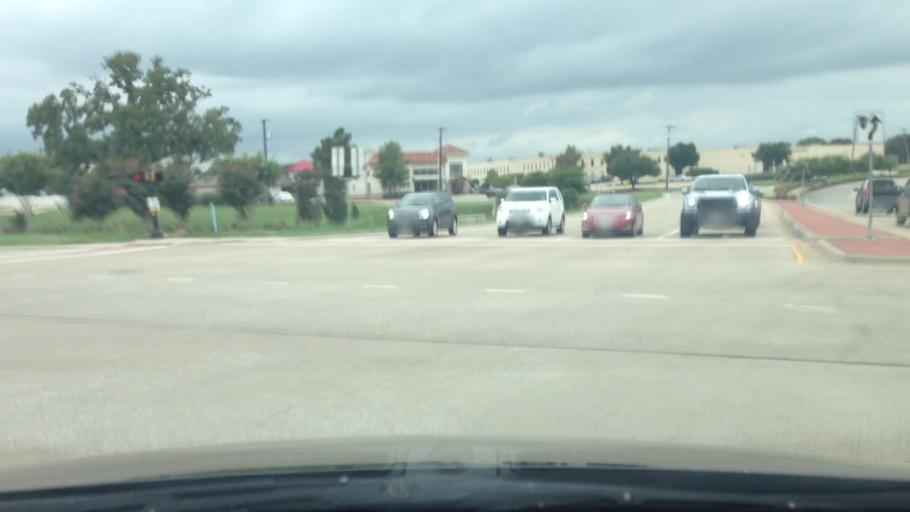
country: US
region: Texas
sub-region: Tarrant County
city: Grapevine
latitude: 32.9399
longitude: -97.1017
